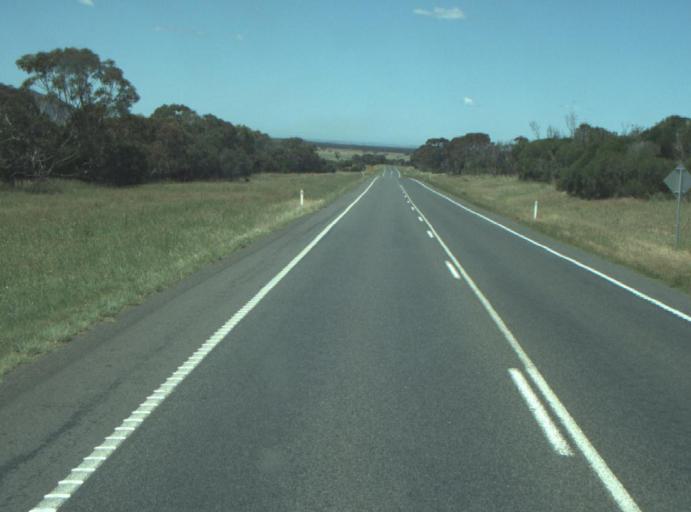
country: AU
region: Victoria
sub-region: Greater Geelong
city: Lara
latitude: -37.8954
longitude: 144.3680
